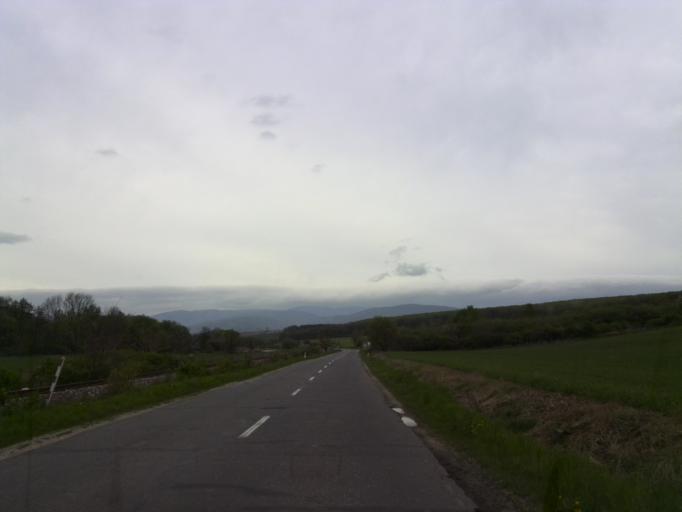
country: SK
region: Kosicky
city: Moldava nad Bodvou
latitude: 48.6471
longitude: 21.0066
